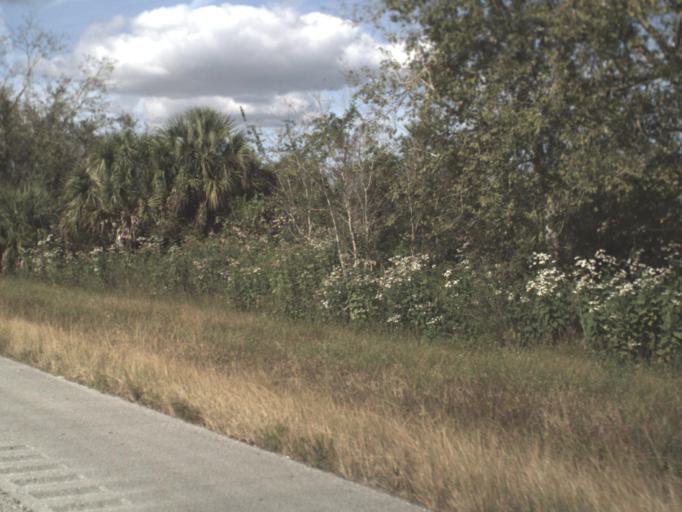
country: US
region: Florida
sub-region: Brevard County
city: Port Saint John
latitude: 28.4403
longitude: -80.8633
